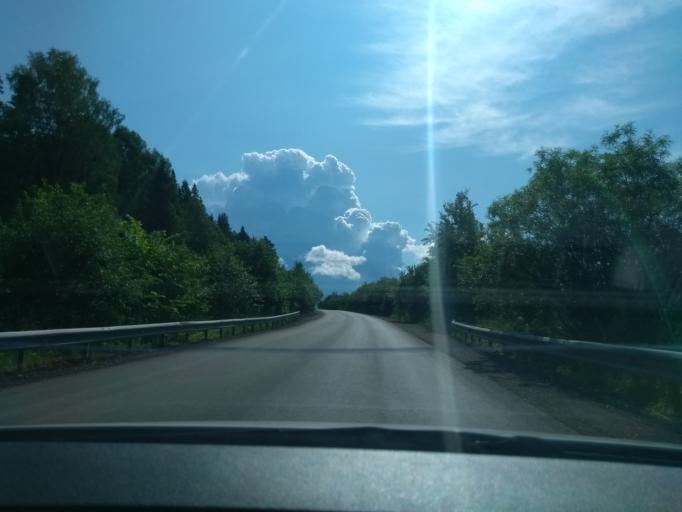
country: RU
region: Perm
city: Kukushtan
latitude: 57.8157
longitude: 56.5434
